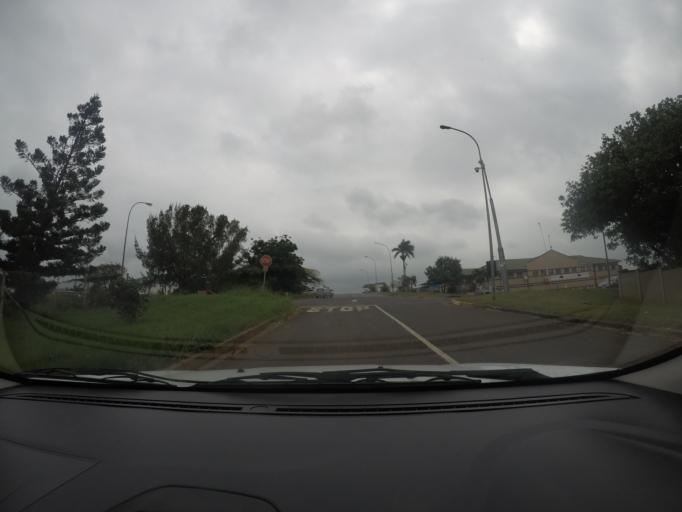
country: ZA
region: KwaZulu-Natal
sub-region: uThungulu District Municipality
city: Empangeni
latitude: -28.7383
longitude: 31.8950
